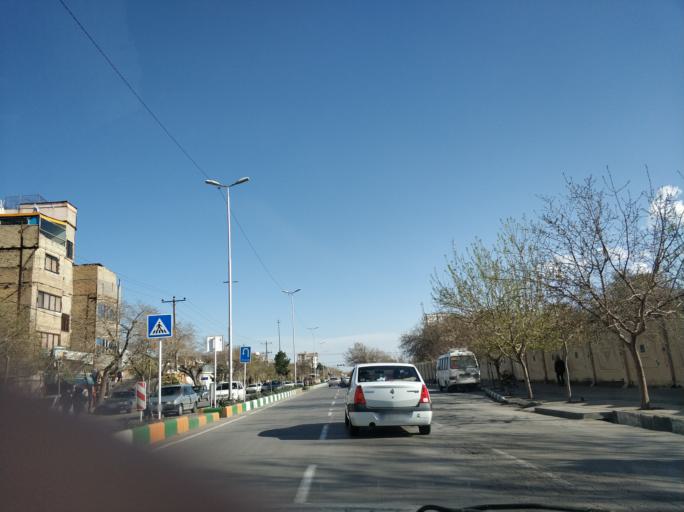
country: IR
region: Razavi Khorasan
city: Mashhad
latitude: 36.3007
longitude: 59.6322
